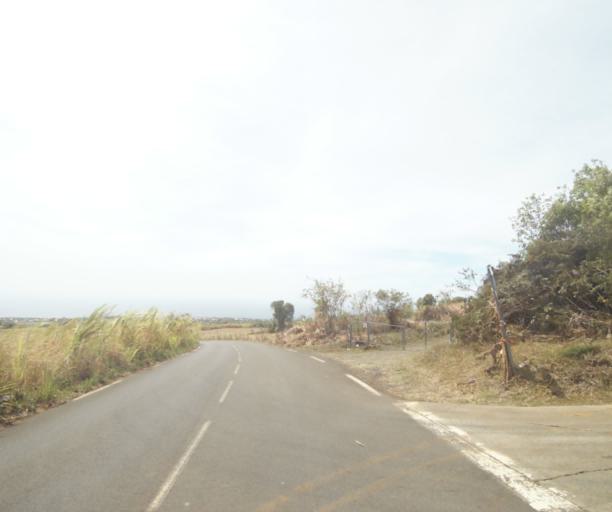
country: RE
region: Reunion
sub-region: Reunion
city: Trois-Bassins
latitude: -21.0673
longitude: 55.2866
